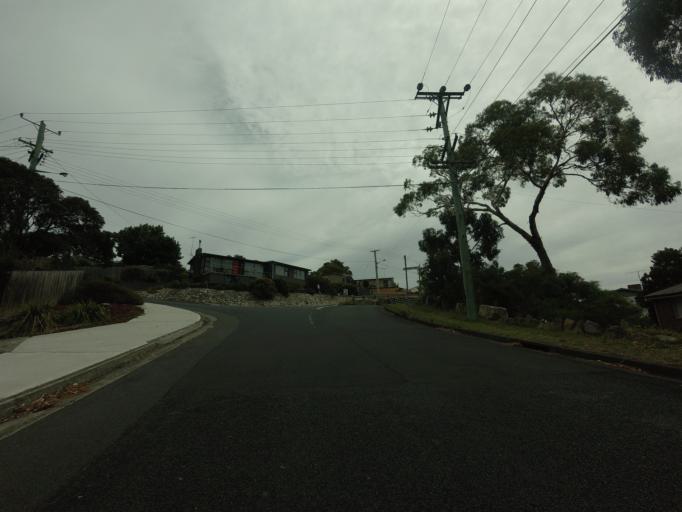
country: AU
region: Tasmania
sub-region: Sorell
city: Sorell
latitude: -42.7959
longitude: 147.5356
